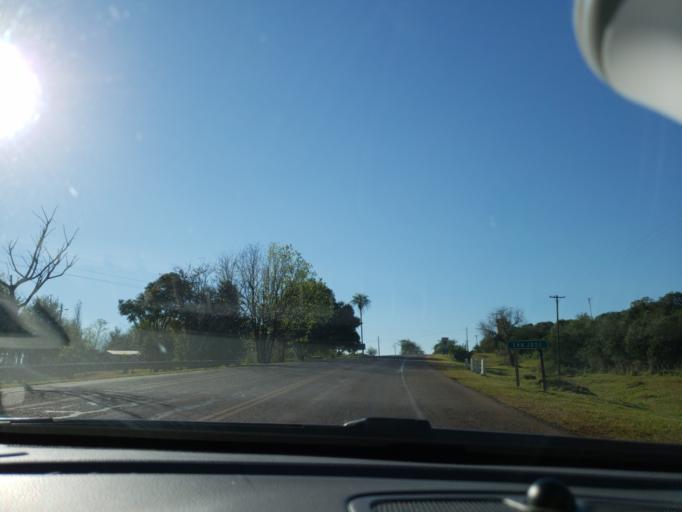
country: AR
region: Misiones
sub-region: Departamento de Apostoles
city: San Jose
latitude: -27.7750
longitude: -55.7734
